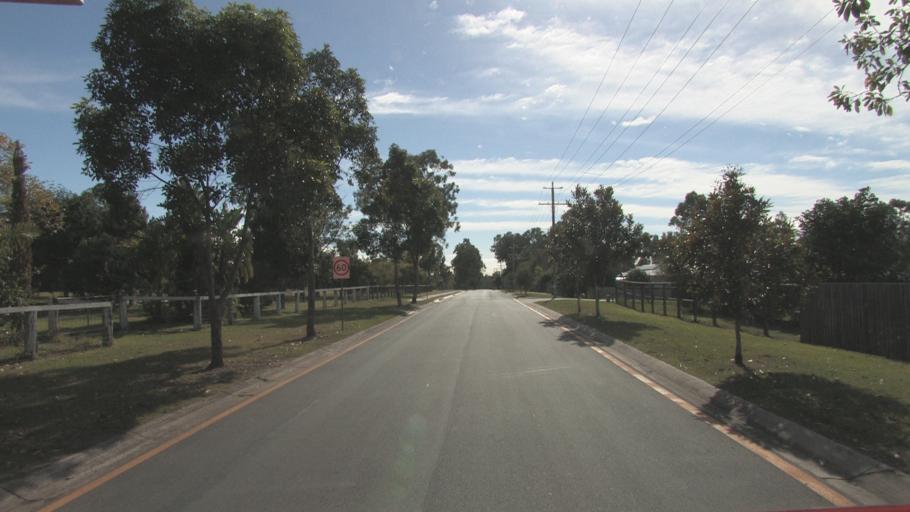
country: AU
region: Queensland
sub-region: Brisbane
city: Forest Lake
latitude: -27.6579
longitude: 152.9945
